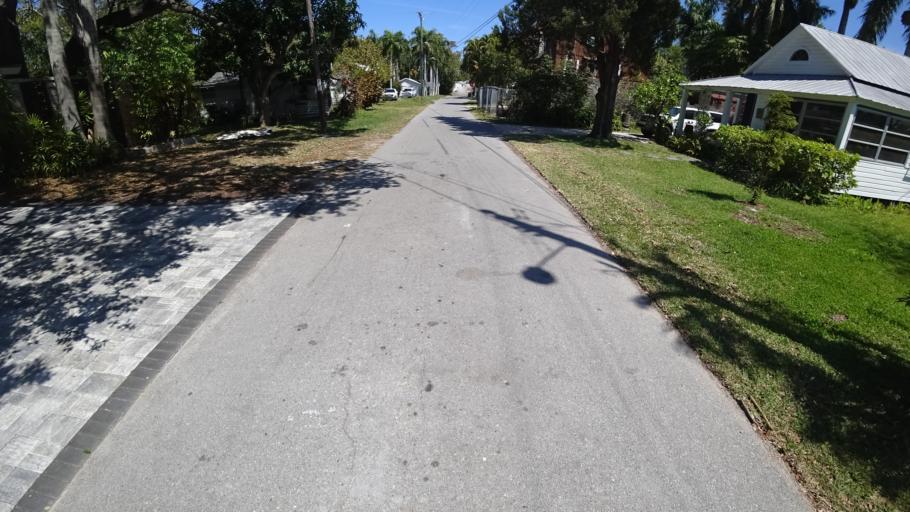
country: US
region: Florida
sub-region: Manatee County
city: Cortez
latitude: 27.4671
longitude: -82.6835
